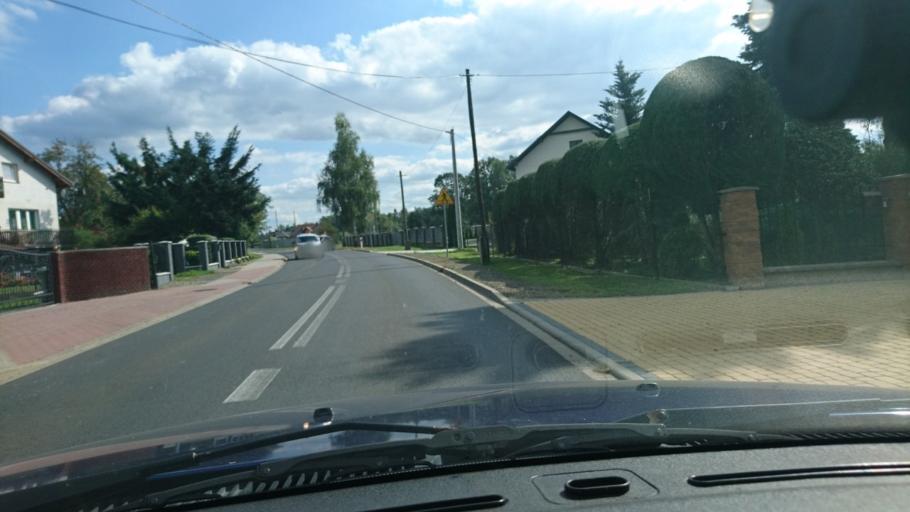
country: PL
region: Silesian Voivodeship
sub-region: Powiat bielski
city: Mazancowice
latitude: 49.8618
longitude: 18.9733
